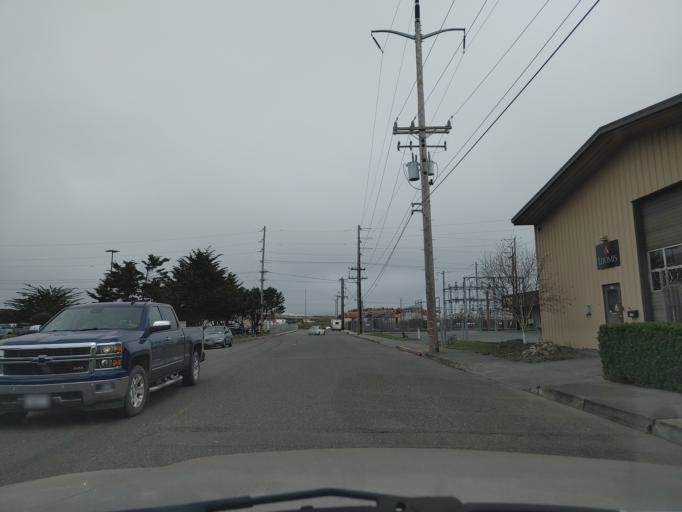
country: US
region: California
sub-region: Humboldt County
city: Eureka
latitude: 40.7920
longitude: -124.1806
